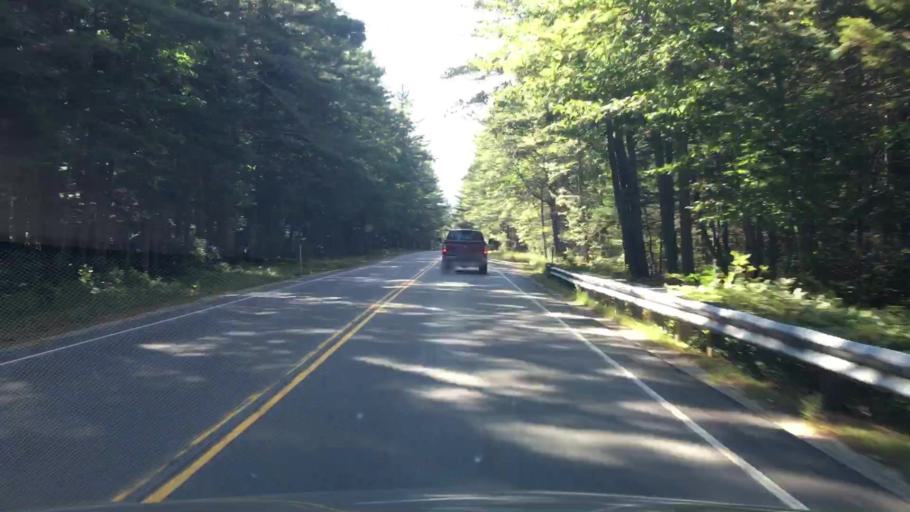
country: US
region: New Hampshire
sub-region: Carroll County
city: Tamworth
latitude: 43.9961
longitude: -71.3461
